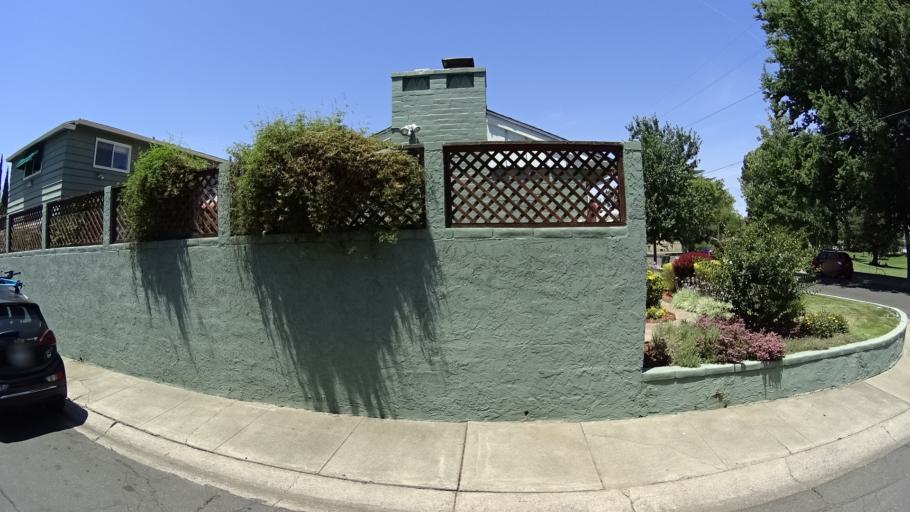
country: US
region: California
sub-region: Sacramento County
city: Sacramento
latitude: 38.5631
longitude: -121.4419
